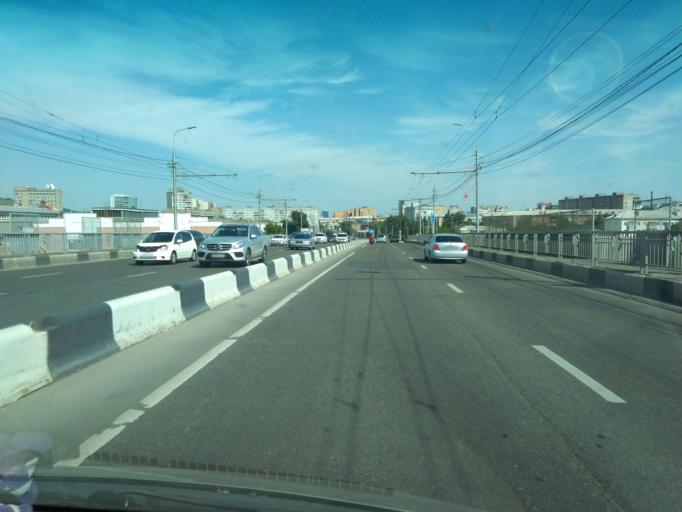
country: RU
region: Krasnoyarskiy
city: Krasnoyarsk
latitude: 56.0125
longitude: 92.8315
